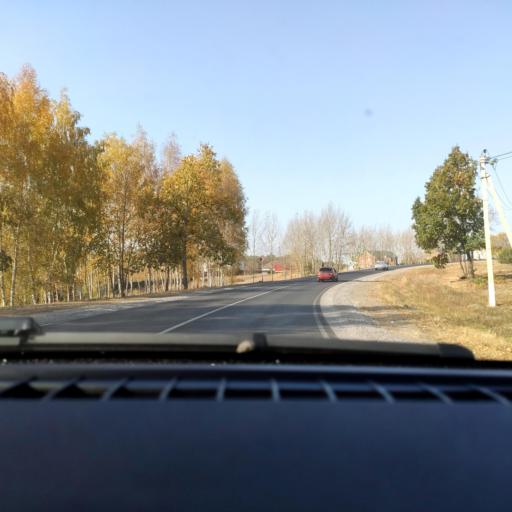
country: RU
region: Voronezj
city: Novaya Usman'
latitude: 51.6799
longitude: 39.3987
